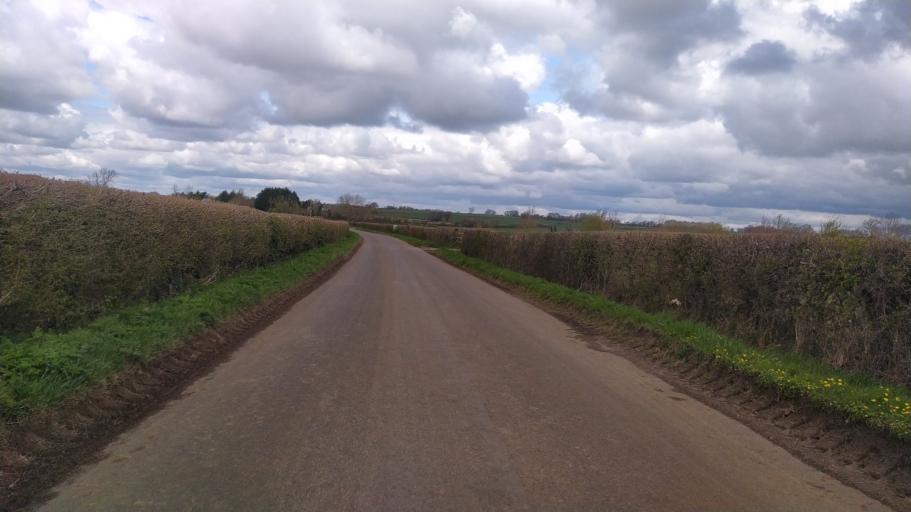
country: GB
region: England
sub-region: Wiltshire
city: Bratton
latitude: 51.2859
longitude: -2.1395
